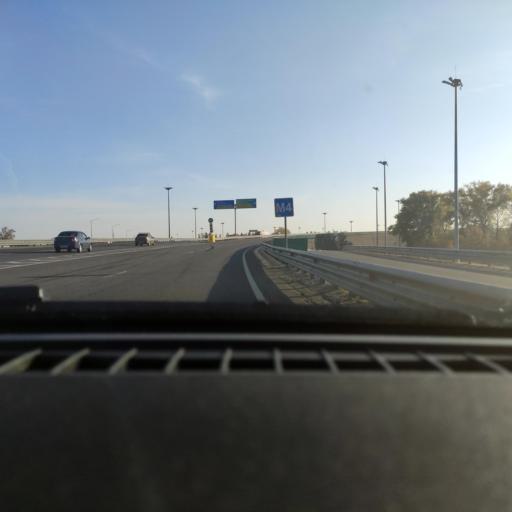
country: RU
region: Voronezj
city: Novaya Usman'
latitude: 51.6544
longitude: 39.3029
